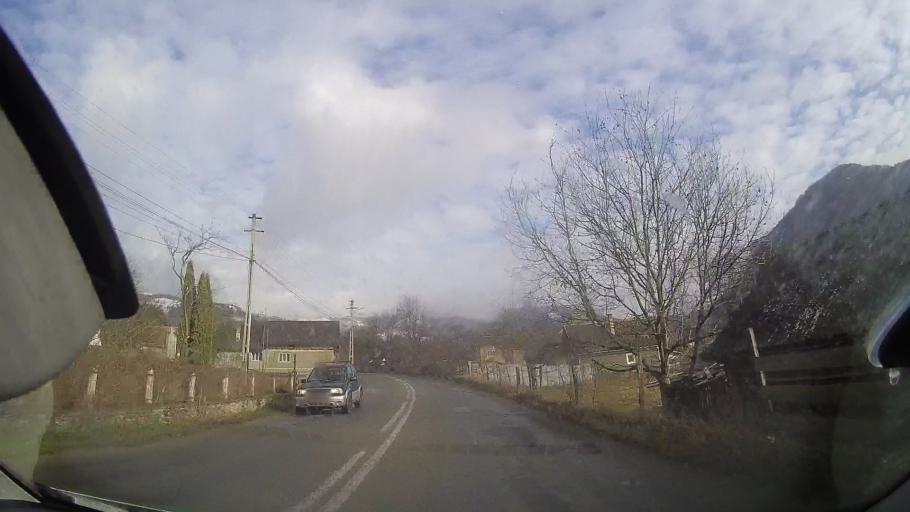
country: RO
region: Alba
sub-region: Comuna Lupsa
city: Lupsa
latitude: 46.3705
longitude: 23.2094
